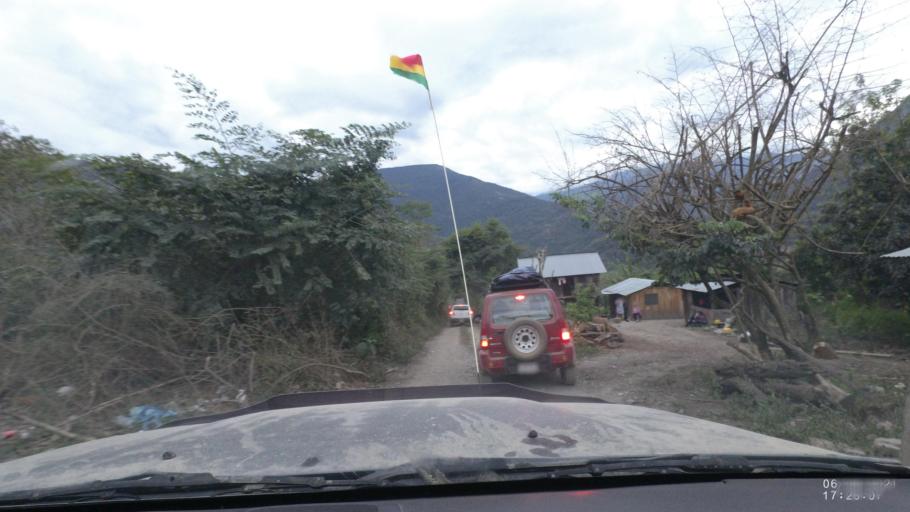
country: BO
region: La Paz
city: Quime
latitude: -16.4777
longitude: -66.7842
